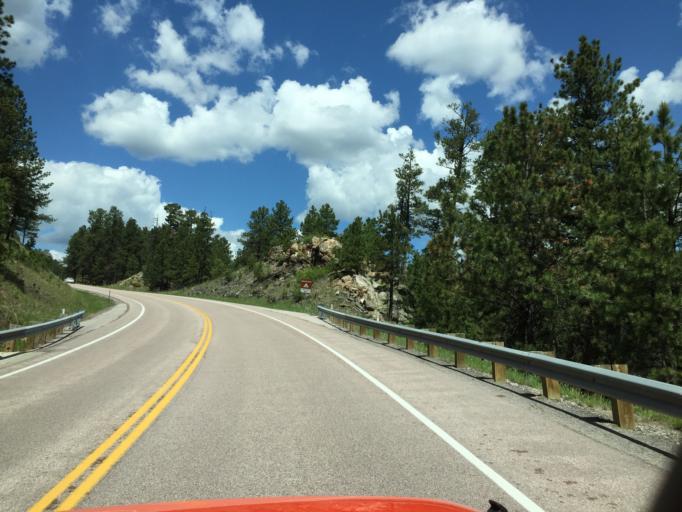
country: US
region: South Dakota
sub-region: Custer County
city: Custer
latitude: 43.8952
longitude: -103.4798
